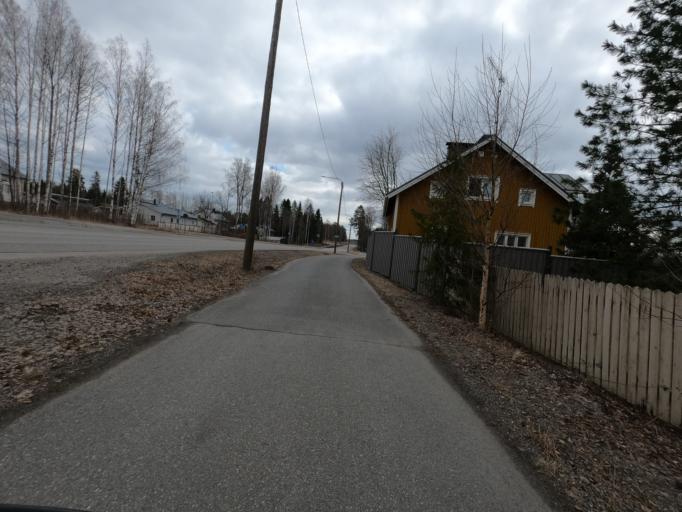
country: FI
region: North Karelia
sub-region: Joensuu
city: Joensuu
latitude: 62.5643
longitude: 29.8117
